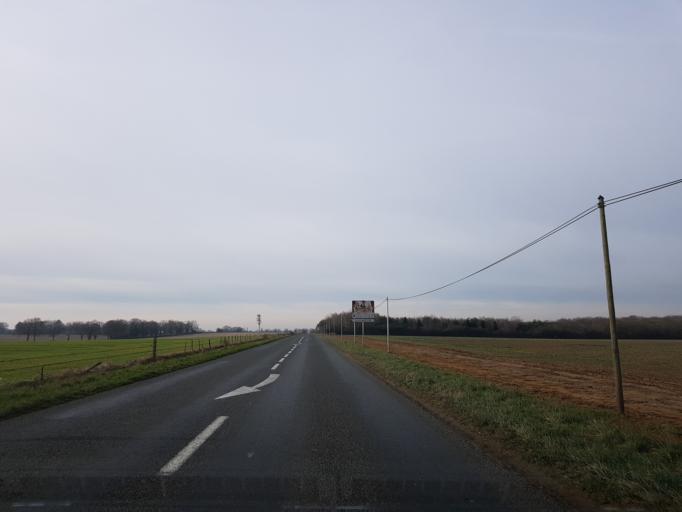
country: FR
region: Auvergne
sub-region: Departement de l'Allier
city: Yzeure
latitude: 46.5780
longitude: 3.4043
